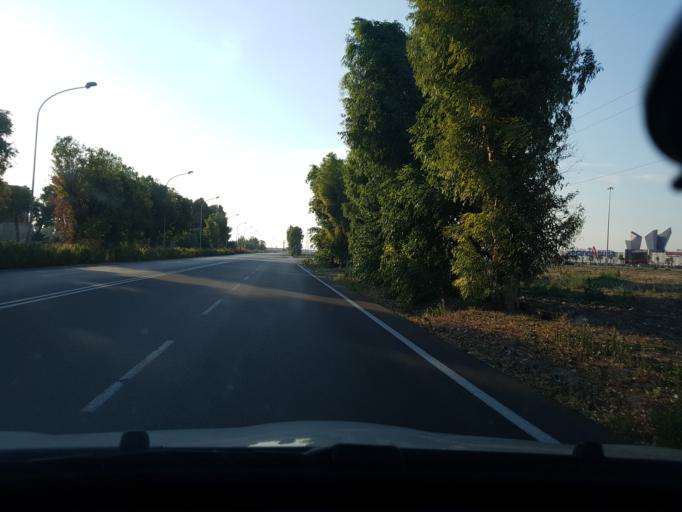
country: IT
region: Apulia
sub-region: Provincia di Foggia
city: Carapelle
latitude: 41.4119
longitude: 15.6522
